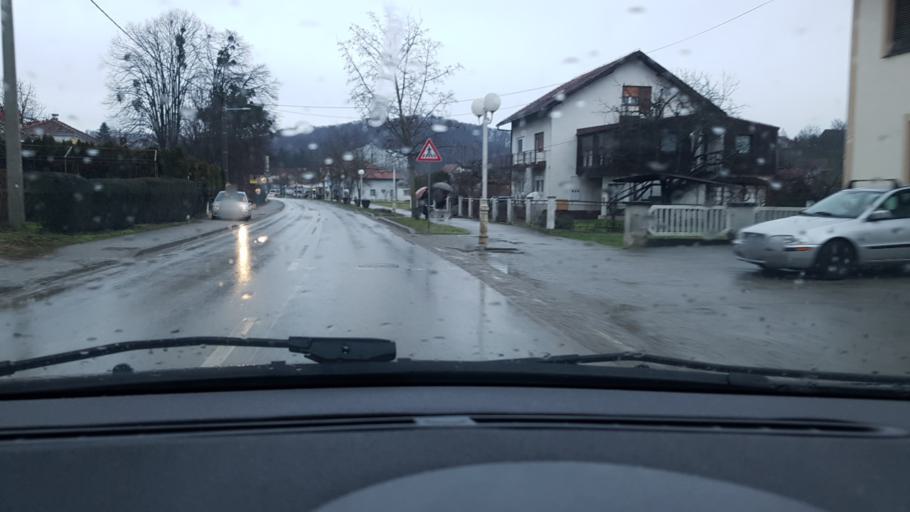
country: HR
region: Krapinsko-Zagorska
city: Oroslavje
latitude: 45.9763
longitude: 15.9284
